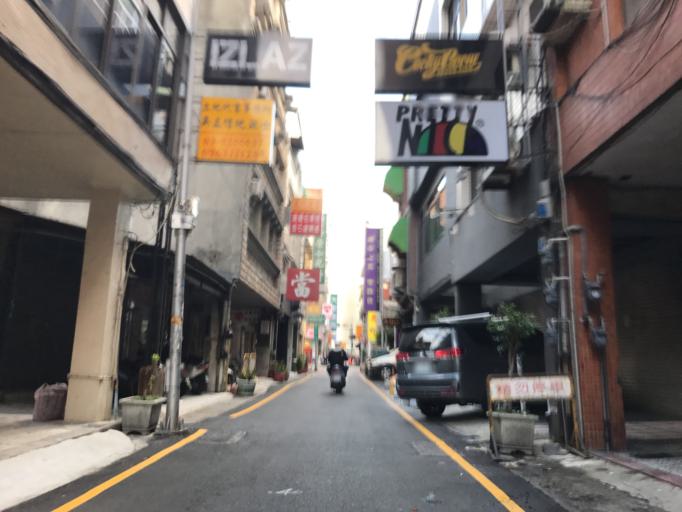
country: TW
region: Taiwan
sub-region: Hsinchu
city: Hsinchu
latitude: 24.8012
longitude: 120.9683
